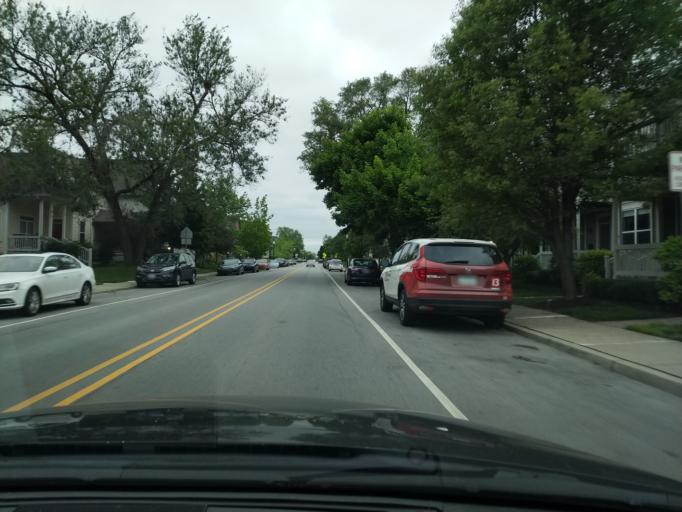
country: US
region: Indiana
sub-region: Marion County
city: Indianapolis
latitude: 39.8011
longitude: -86.1496
